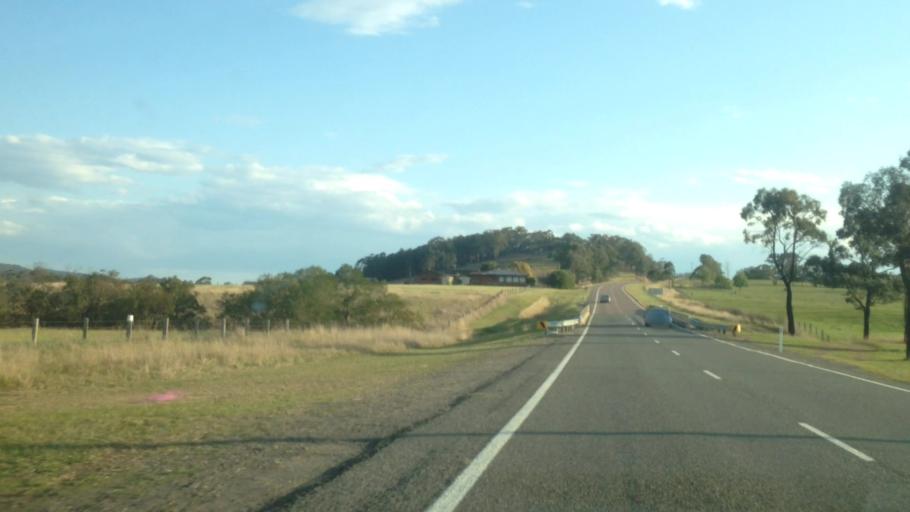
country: AU
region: New South Wales
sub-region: Cessnock
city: Kurri Kurri
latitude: -32.8777
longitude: 151.4745
